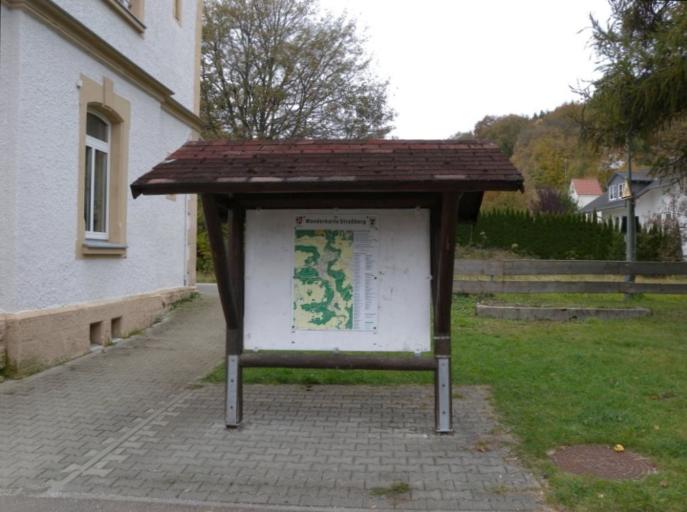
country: DE
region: Baden-Wuerttemberg
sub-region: Tuebingen Region
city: Strassberg
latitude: 48.1789
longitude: 9.0880
